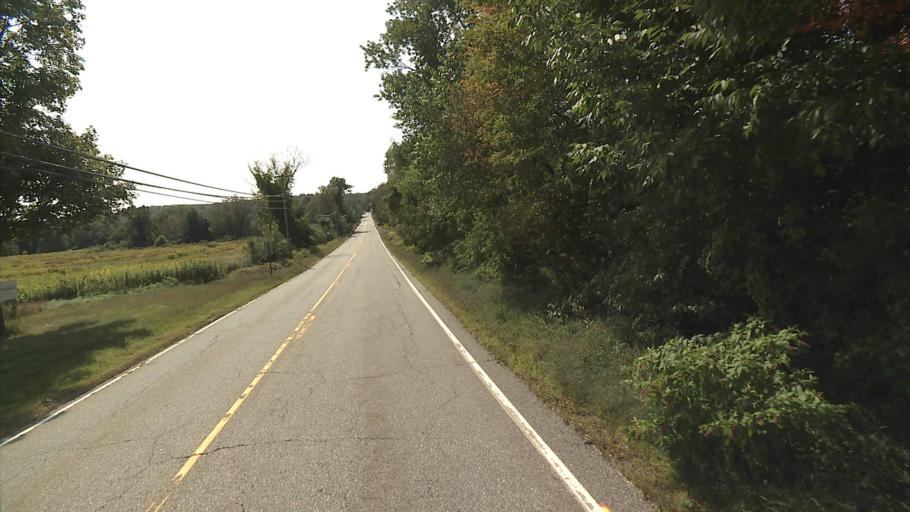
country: US
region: Connecticut
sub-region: Windham County
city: Putnam
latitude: 41.8627
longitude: -71.9593
